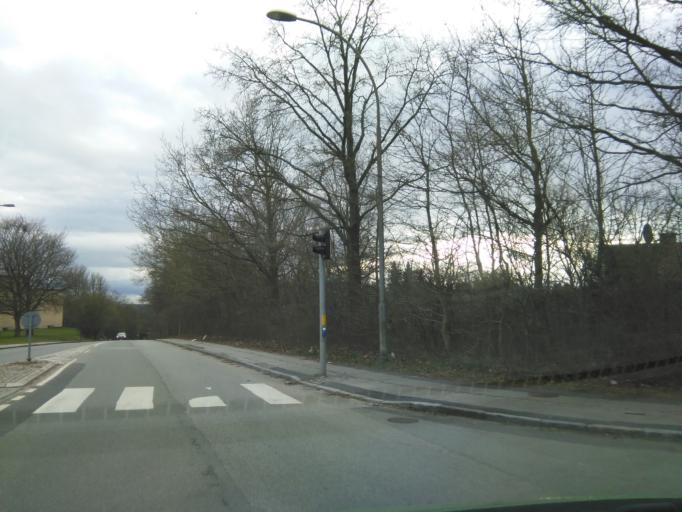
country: DK
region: Central Jutland
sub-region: Arhus Kommune
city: Stavtrup
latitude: 56.1599
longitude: 10.1288
